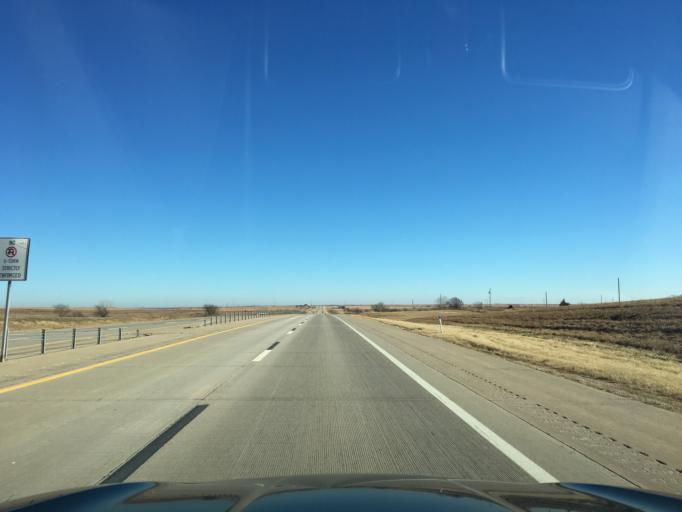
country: US
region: Oklahoma
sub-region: Noble County
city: Perry
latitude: 36.3920
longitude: -97.1512
